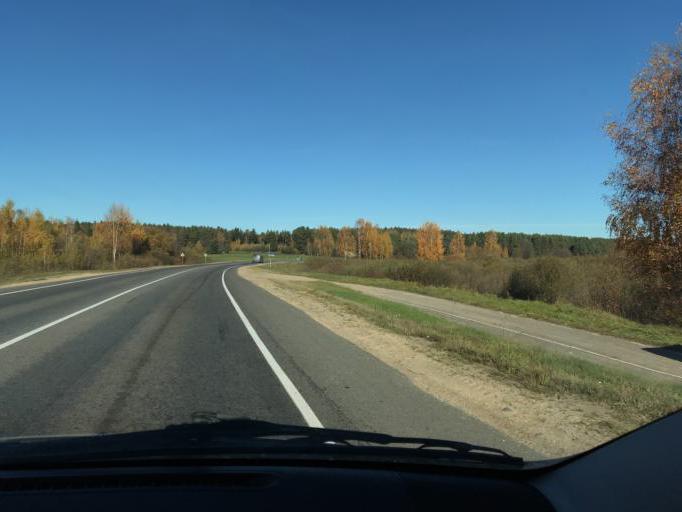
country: BY
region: Vitebsk
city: Polatsk
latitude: 55.3127
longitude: 28.7769
